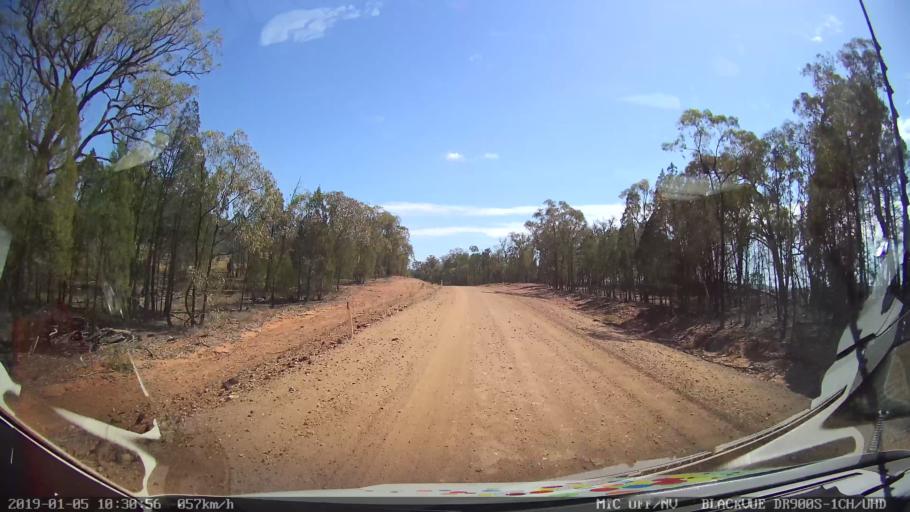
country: AU
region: New South Wales
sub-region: Gilgandra
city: Gilgandra
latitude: -31.5283
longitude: 148.9261
